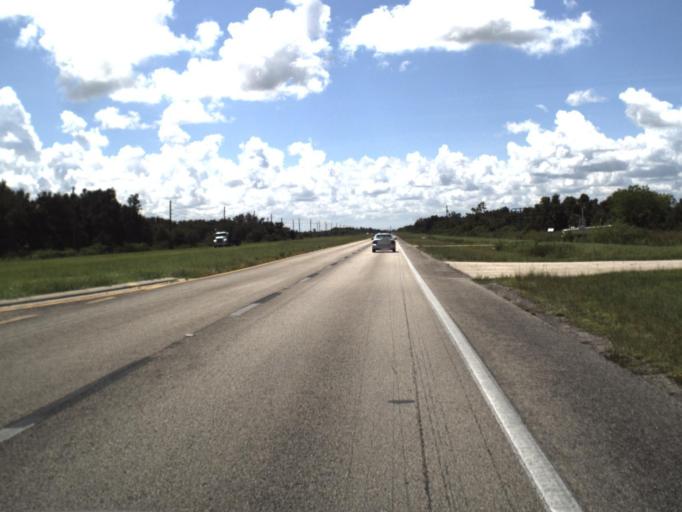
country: US
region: Florida
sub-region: Charlotte County
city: Harbour Heights
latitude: 27.0276
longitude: -81.9587
